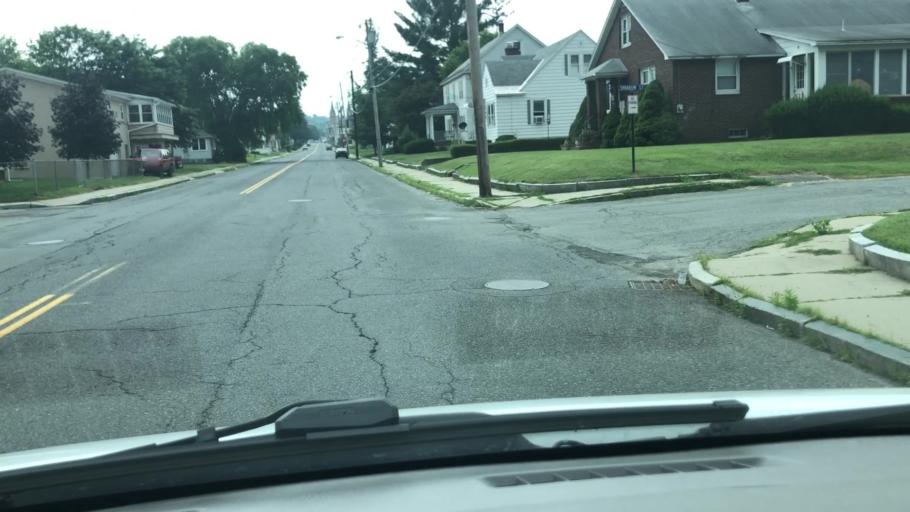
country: US
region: Massachusetts
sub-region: Berkshire County
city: Adams
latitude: 42.6317
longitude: -73.1104
